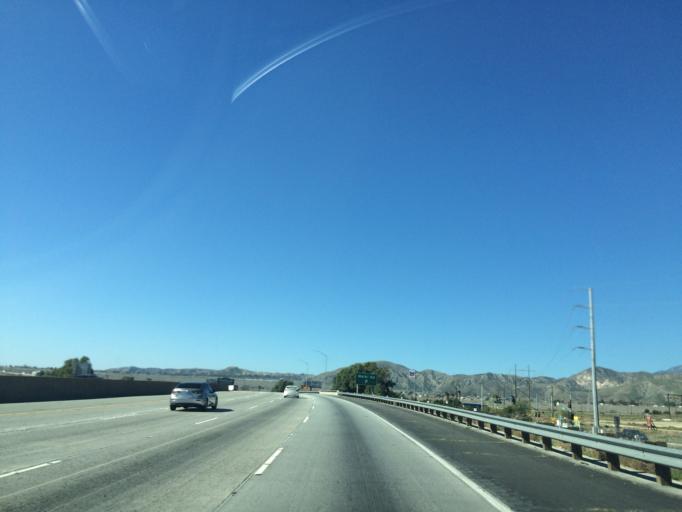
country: US
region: California
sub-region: Riverside County
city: Cabazon
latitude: 33.9306
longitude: -116.8201
